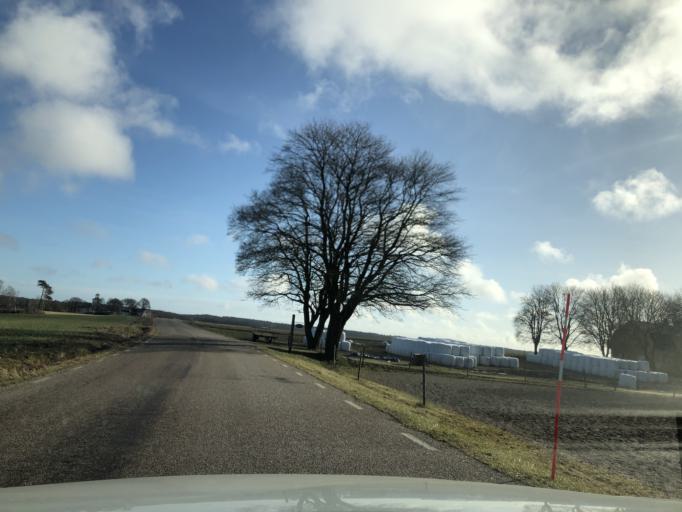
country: SE
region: Vaestra Goetaland
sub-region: Ulricehamns Kommun
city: Ulricehamn
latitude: 57.8002
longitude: 13.5838
